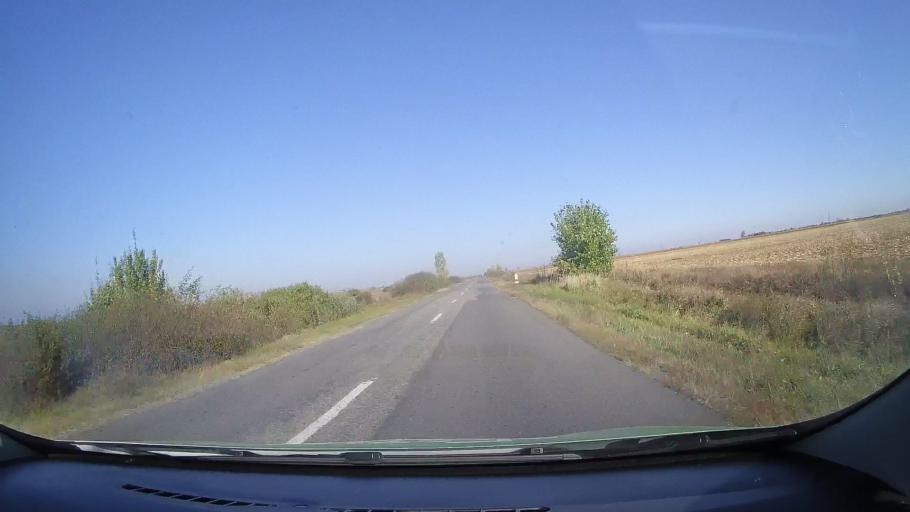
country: RO
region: Satu Mare
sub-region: Comuna Cauas
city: Cauas
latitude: 47.5268
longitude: 22.5681
